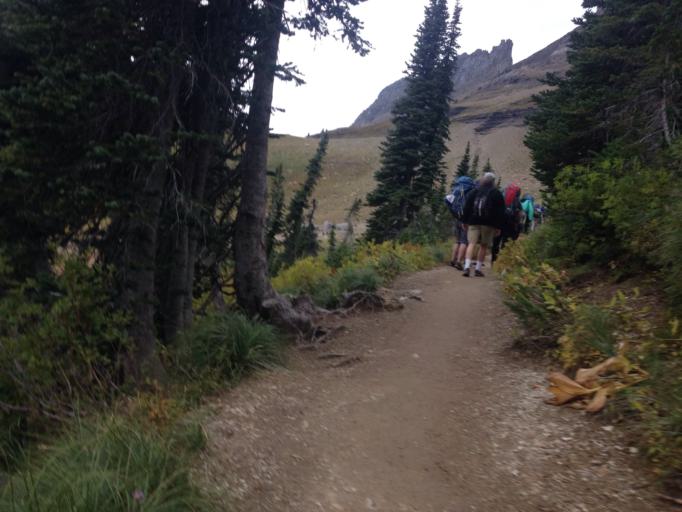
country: US
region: Montana
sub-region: Flathead County
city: Columbia Falls
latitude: 48.7325
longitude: -113.7208
